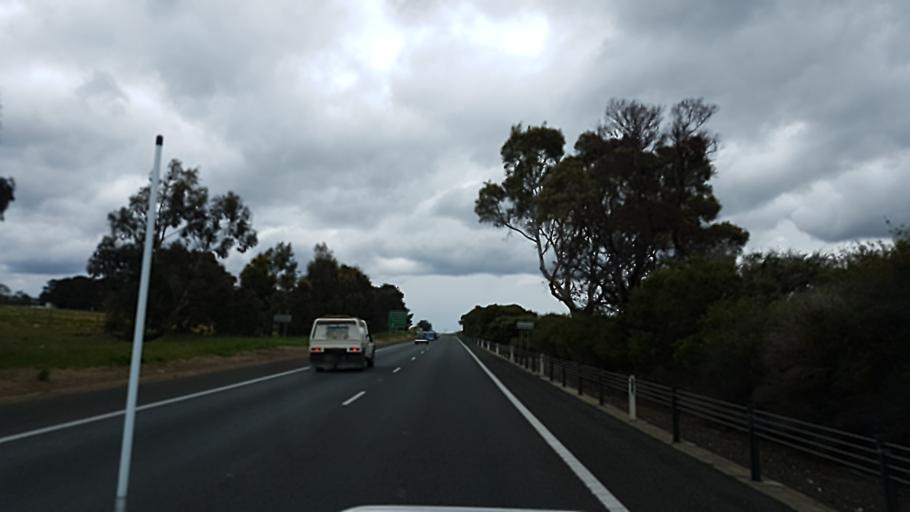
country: AU
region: Victoria
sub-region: Moorabool
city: Bacchus Marsh
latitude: -37.6100
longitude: 144.3110
